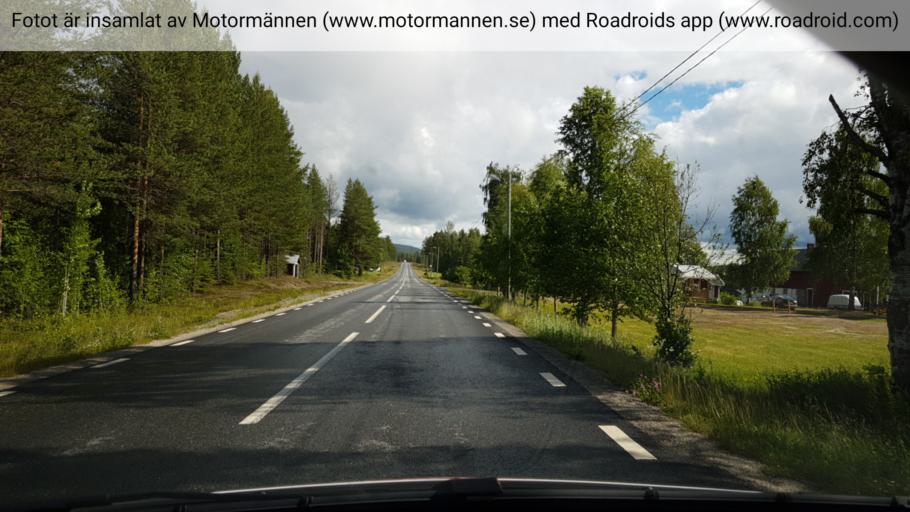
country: SE
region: Vaesterbotten
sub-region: Bjurholms Kommun
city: Bjurholm
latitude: 64.2890
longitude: 19.1958
